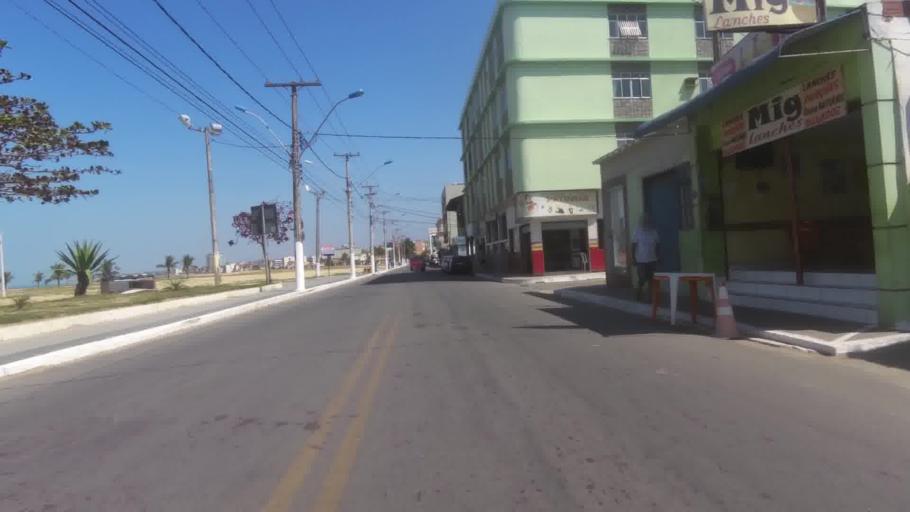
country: BR
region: Espirito Santo
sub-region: Marataizes
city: Marataizes
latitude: -21.0430
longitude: -40.8260
